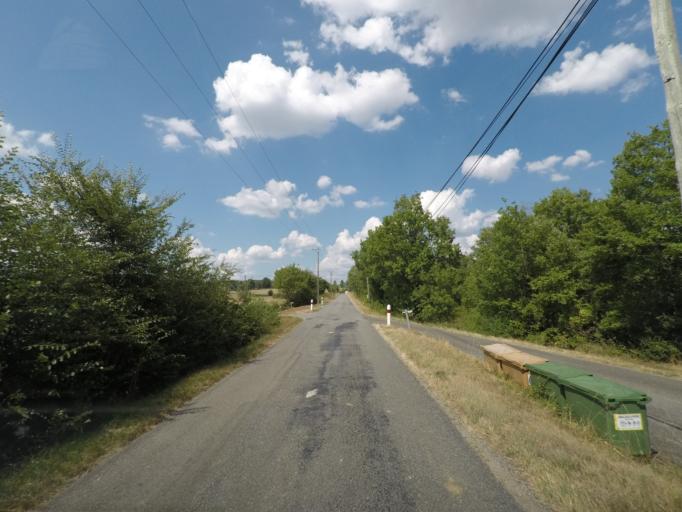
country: FR
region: Midi-Pyrenees
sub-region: Departement du Lot
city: Cahors
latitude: 44.5776
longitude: 1.5780
